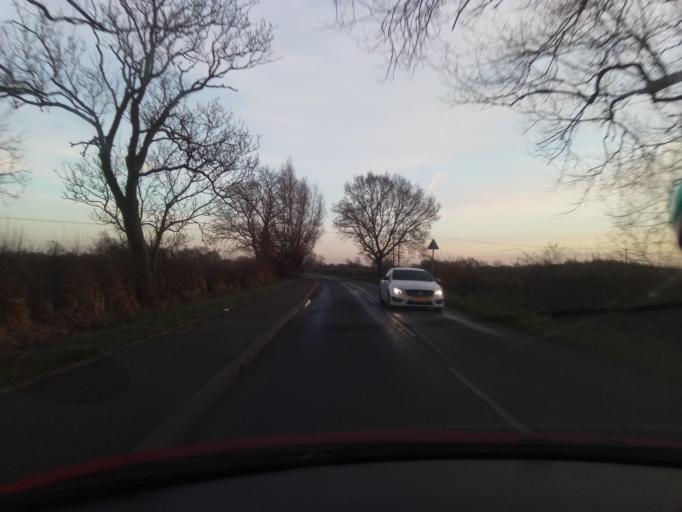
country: GB
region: England
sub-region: Leicestershire
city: Sileby
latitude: 52.7326
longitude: -1.1283
